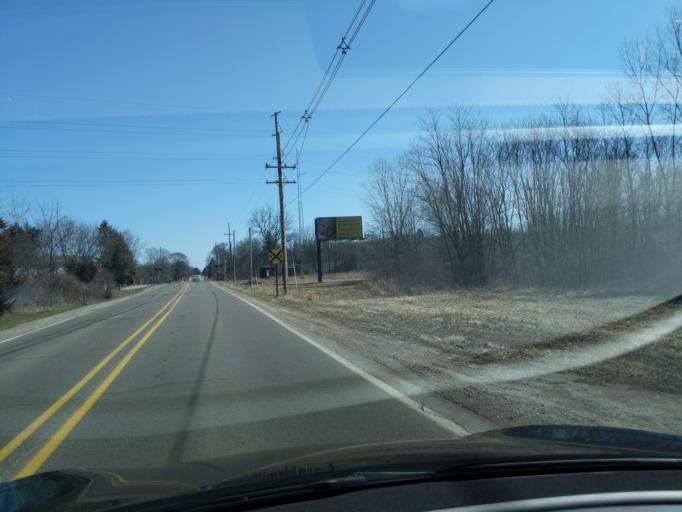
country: US
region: Michigan
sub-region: Ingham County
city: Holt
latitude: 42.6547
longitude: -84.5138
